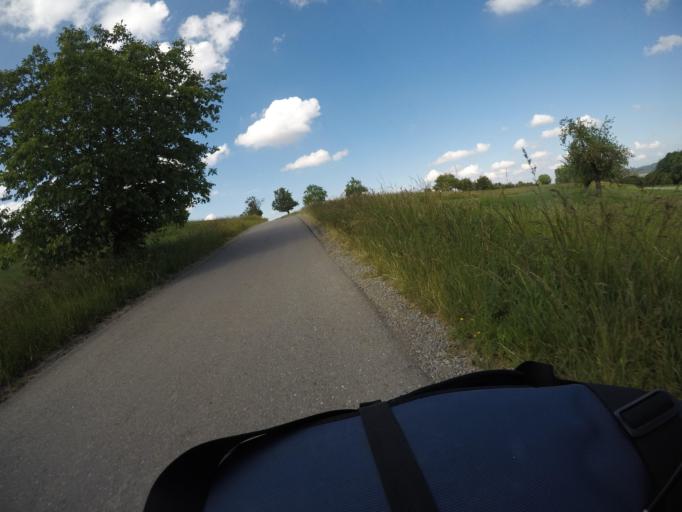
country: DE
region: Baden-Wuerttemberg
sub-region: Regierungsbezirk Stuttgart
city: Herrenberg
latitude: 48.6023
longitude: 8.8339
